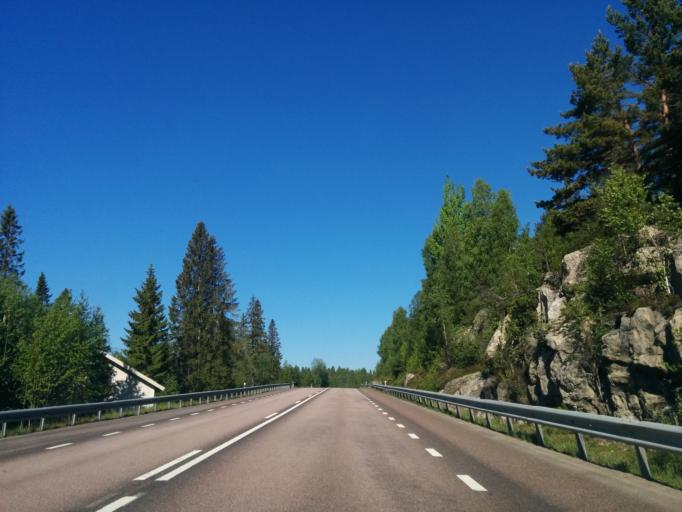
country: SE
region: Vaesternorrland
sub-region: Haernoesands Kommun
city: Haernoesand
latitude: 62.7928
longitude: 17.9053
